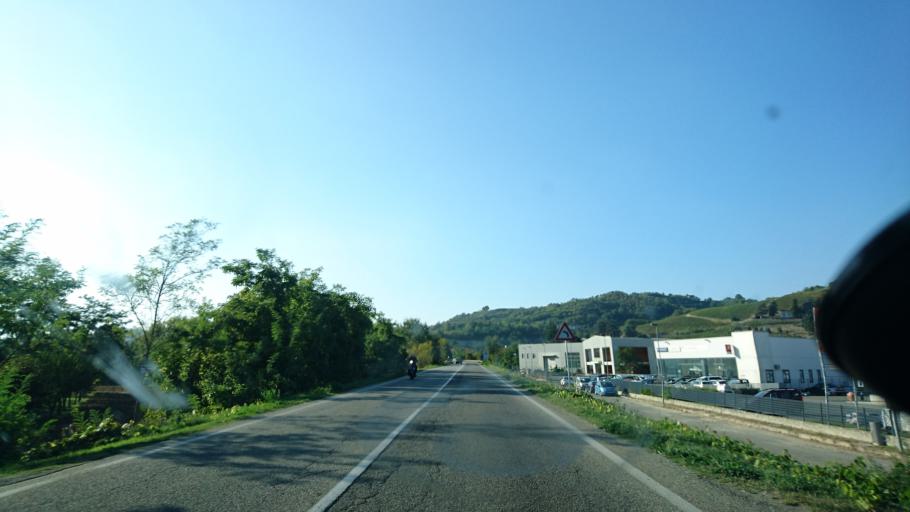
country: IT
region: Piedmont
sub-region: Provincia di Alessandria
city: Terzo
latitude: 44.6737
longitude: 8.4424
